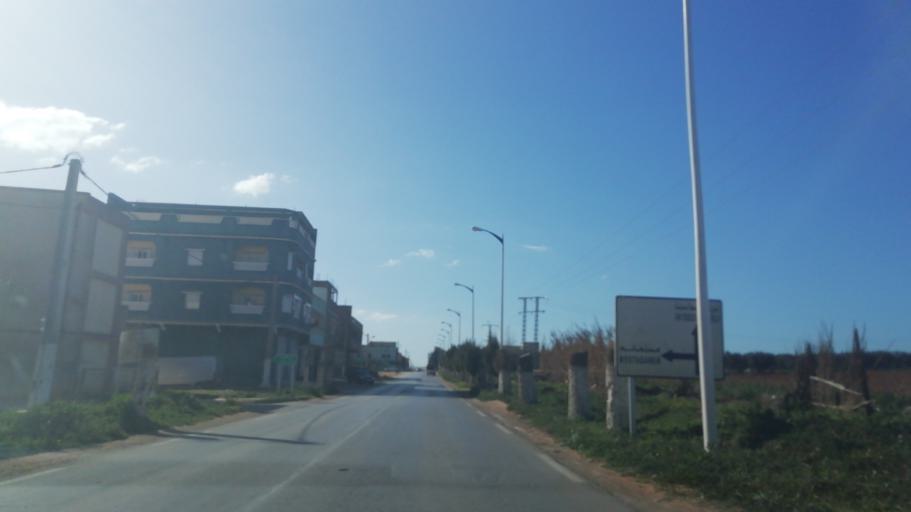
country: DZ
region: Mostaganem
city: Mostaganem
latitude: 35.9996
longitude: 0.3072
